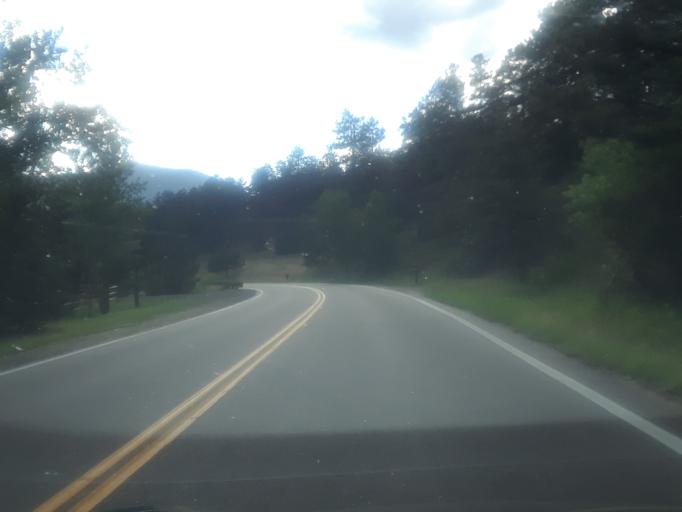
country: US
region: Colorado
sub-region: Jefferson County
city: Kittredge
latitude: 39.7170
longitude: -105.3806
